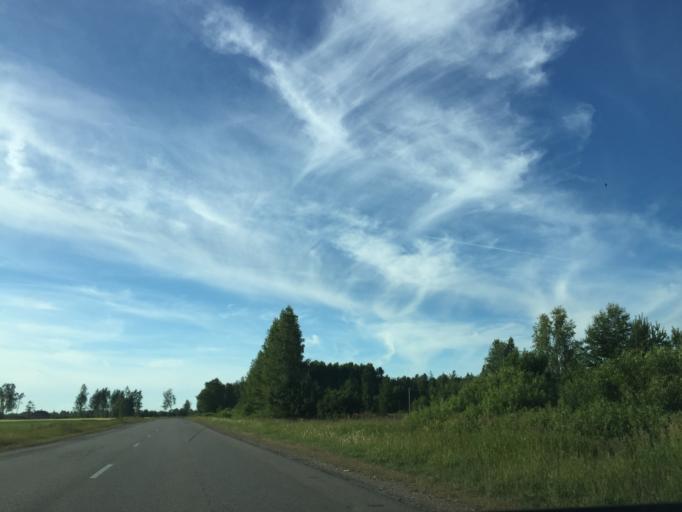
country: LV
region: Ventspils
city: Ventspils
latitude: 57.2906
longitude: 21.5652
